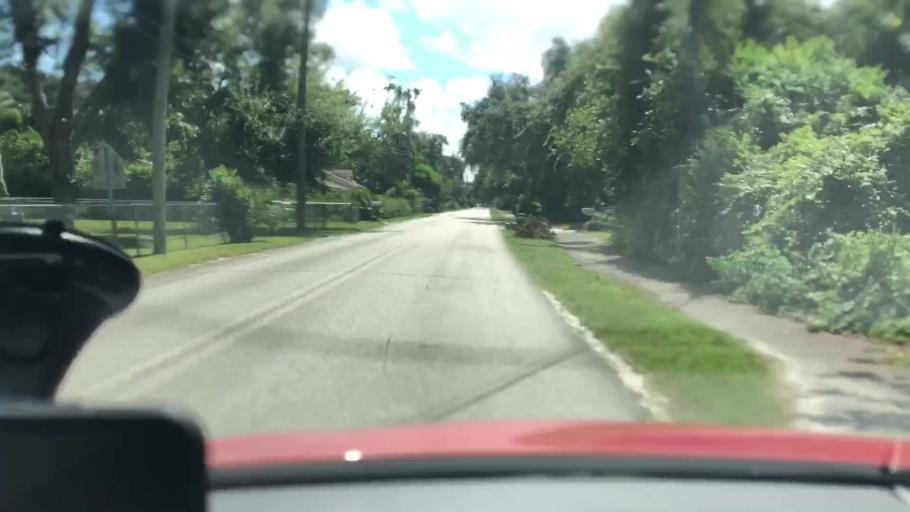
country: US
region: Florida
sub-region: Volusia County
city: New Smyrna Beach
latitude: 29.0097
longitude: -80.9248
